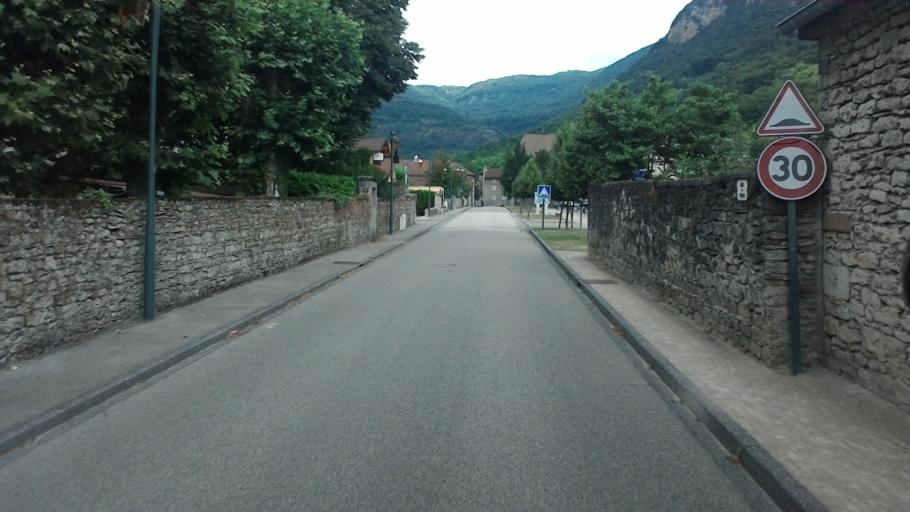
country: FR
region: Rhone-Alpes
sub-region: Departement de l'Ain
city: Villebois
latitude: 45.8469
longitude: 5.4339
